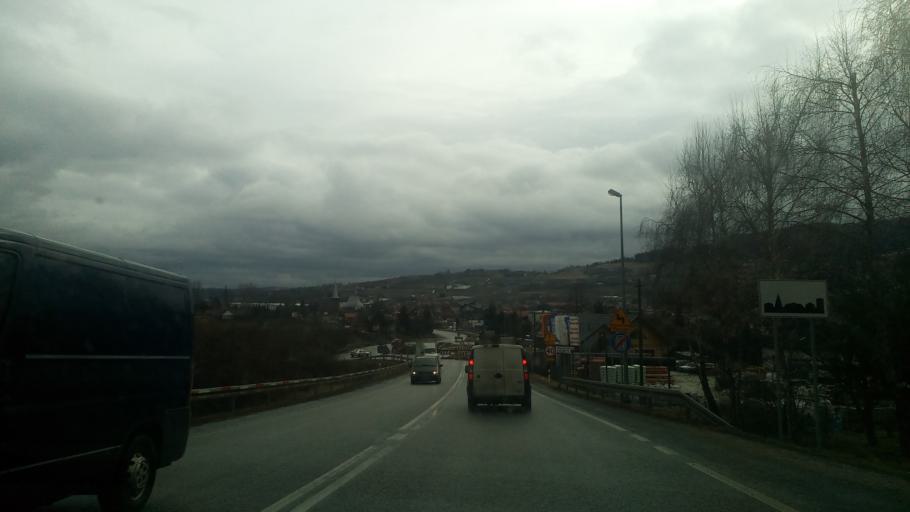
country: PL
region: Lesser Poland Voivodeship
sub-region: Powiat nowosadecki
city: Lososina Dolna
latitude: 49.7150
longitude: 20.6405
